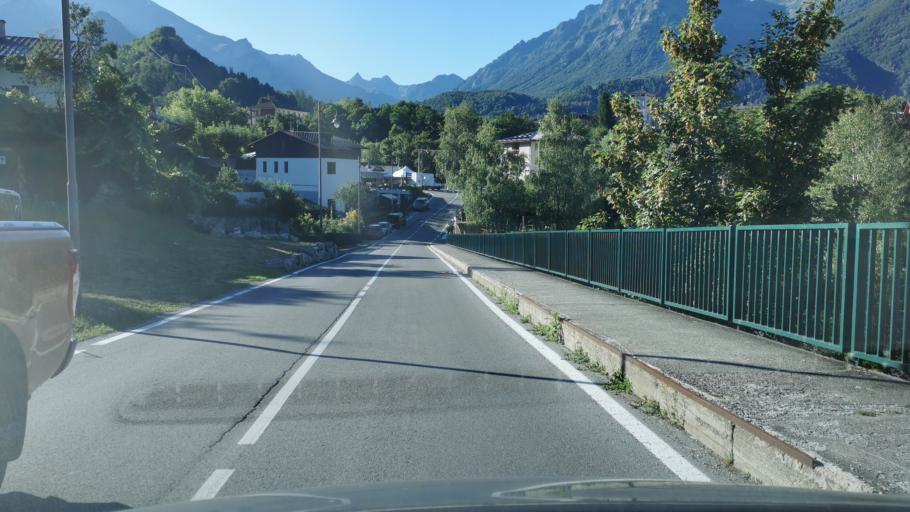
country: IT
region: Piedmont
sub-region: Provincia di Cuneo
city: Entracque
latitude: 44.2406
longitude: 7.3965
